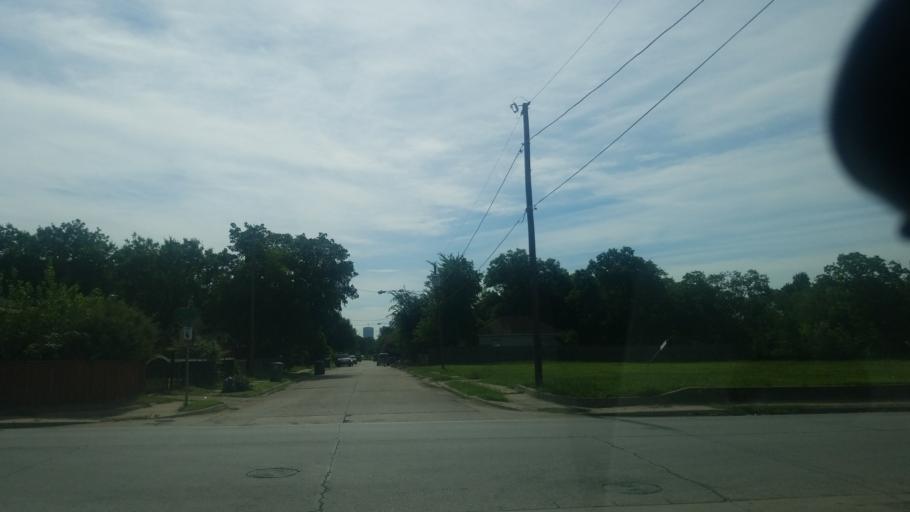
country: US
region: Texas
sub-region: Dallas County
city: Dallas
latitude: 32.7834
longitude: -96.8535
